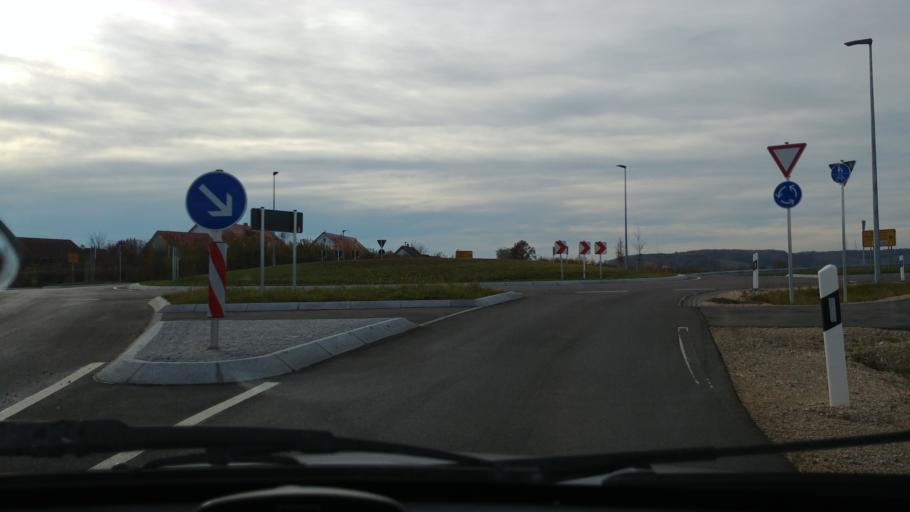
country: DE
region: Bavaria
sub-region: Swabia
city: Bachhagel
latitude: 48.6408
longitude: 10.3229
